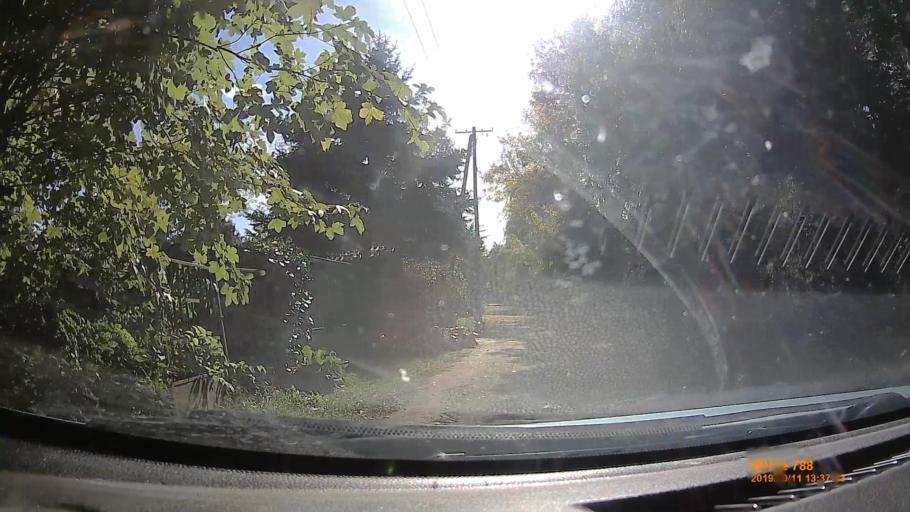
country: HU
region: Hajdu-Bihar
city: Balmazujvaros
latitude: 47.5424
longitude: 21.3275
